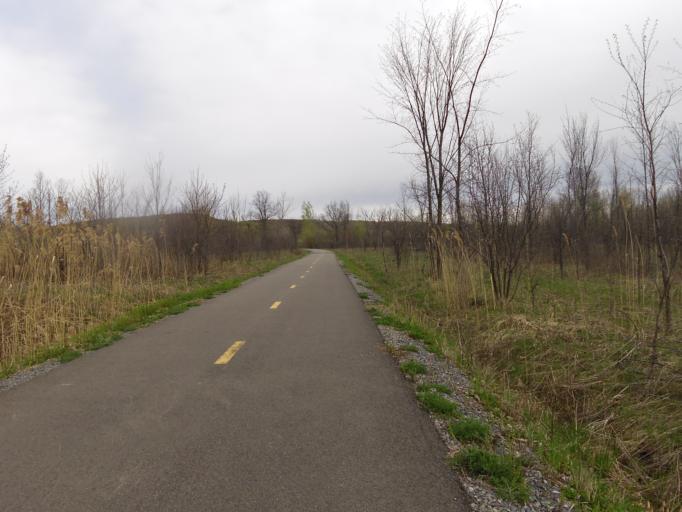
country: CA
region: Quebec
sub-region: Laurentides
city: Sainte-Marthe-sur-le-Lac
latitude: 45.4950
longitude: -73.9991
